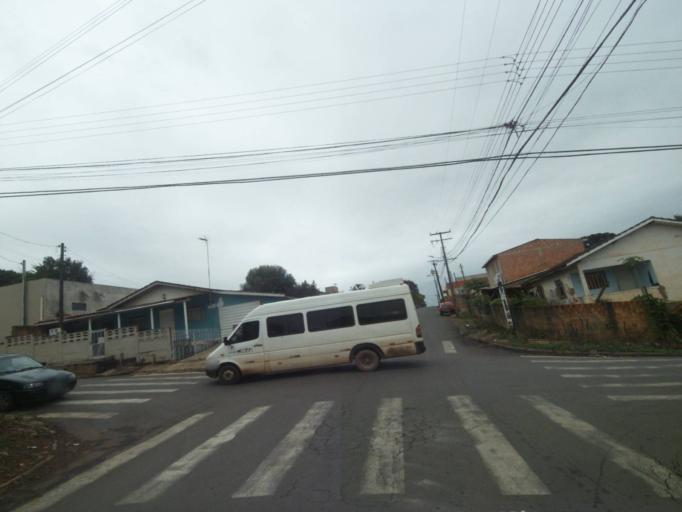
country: BR
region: Parana
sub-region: Telemaco Borba
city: Telemaco Borba
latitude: -24.3232
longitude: -50.6568
